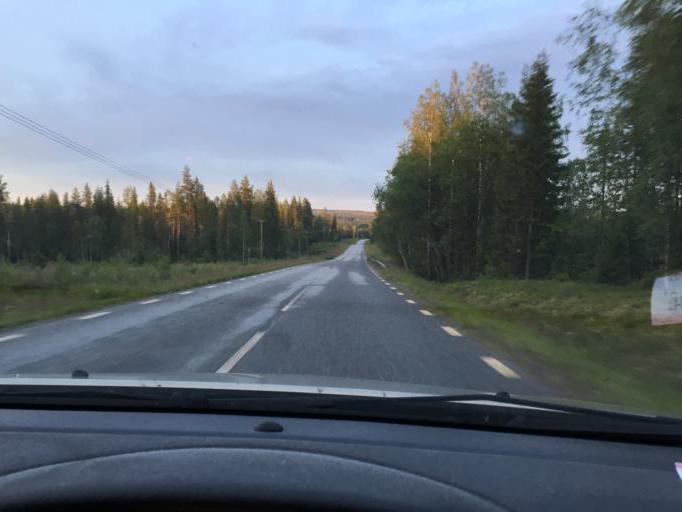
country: SE
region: Norrbotten
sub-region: Kalix Kommun
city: Toere
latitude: 66.0536
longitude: 22.5249
